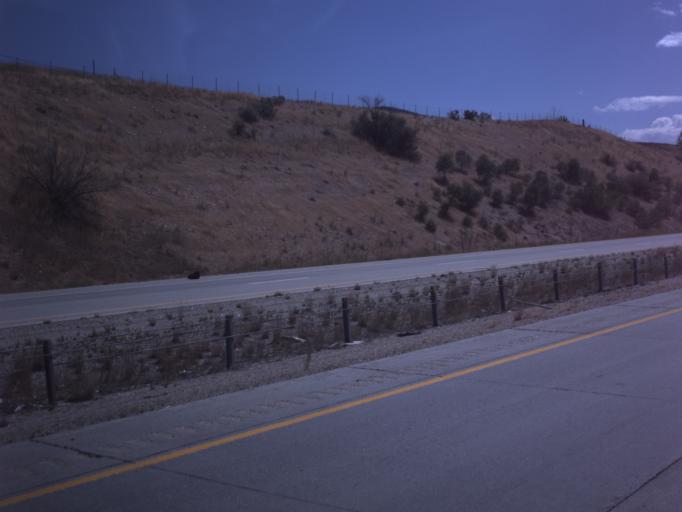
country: US
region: Utah
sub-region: Morgan County
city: Morgan
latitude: 41.0849
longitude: -111.7318
